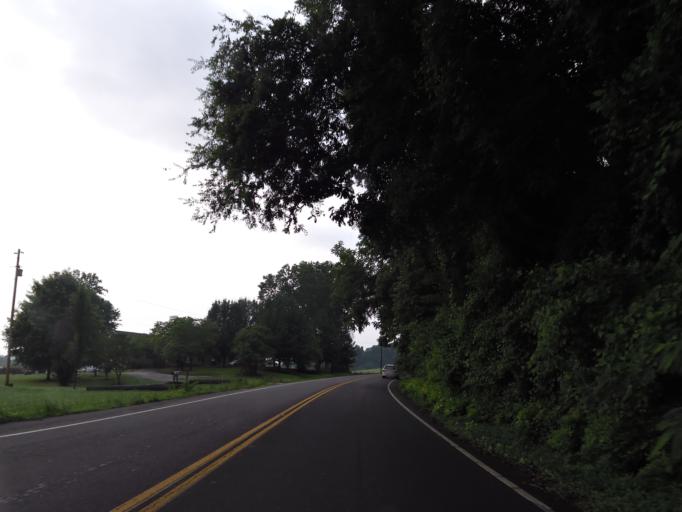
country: US
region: Tennessee
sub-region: Blount County
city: Eagleton Village
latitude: 35.8173
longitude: -83.9363
